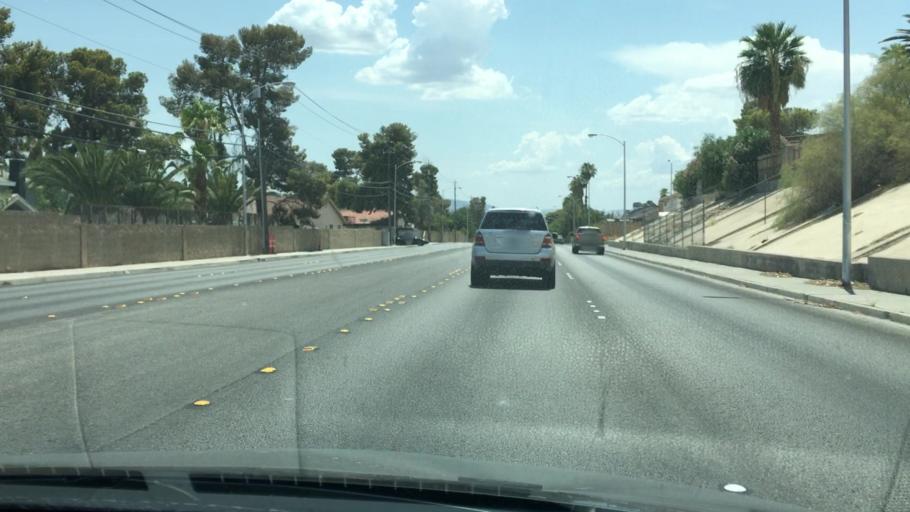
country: US
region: Nevada
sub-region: Clark County
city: Whitney
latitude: 36.0977
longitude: -115.0918
